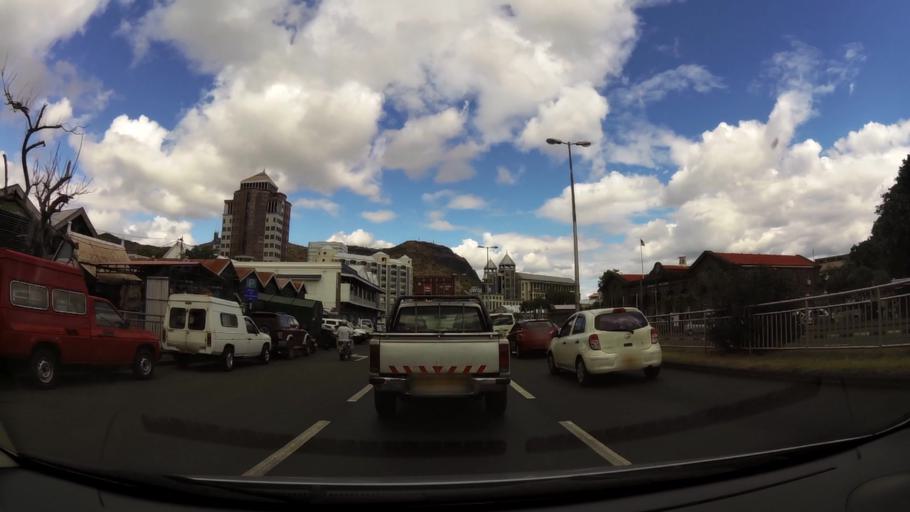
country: MU
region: Port Louis
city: Port Louis
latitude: -20.1599
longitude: 57.5022
